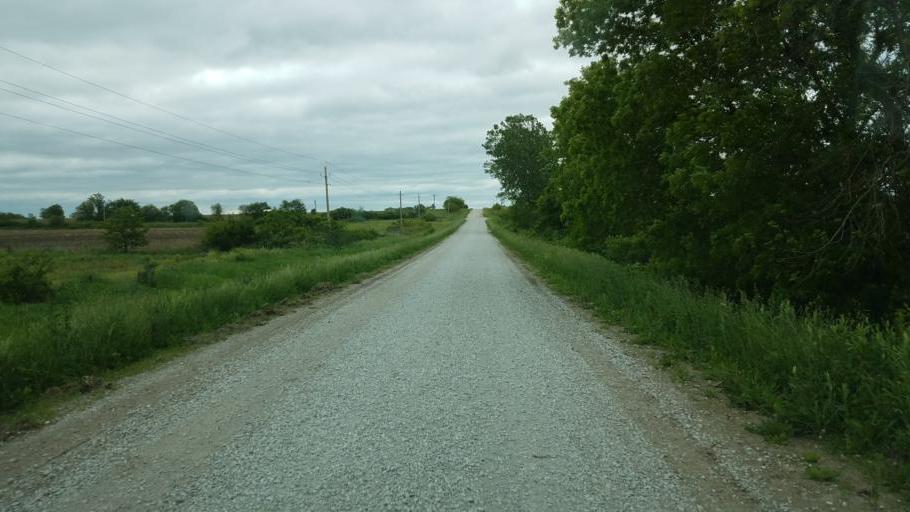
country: US
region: Iowa
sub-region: Decatur County
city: Lamoni
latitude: 40.6527
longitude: -93.9232
